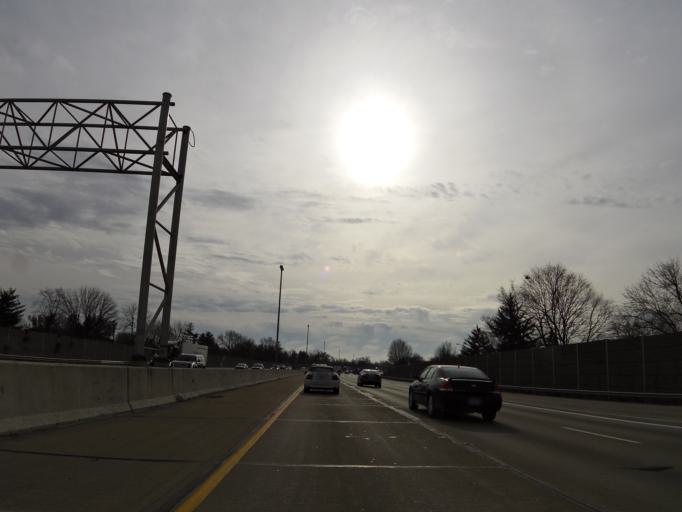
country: US
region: Indiana
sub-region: Marion County
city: Warren Park
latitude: 39.7890
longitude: -86.0336
